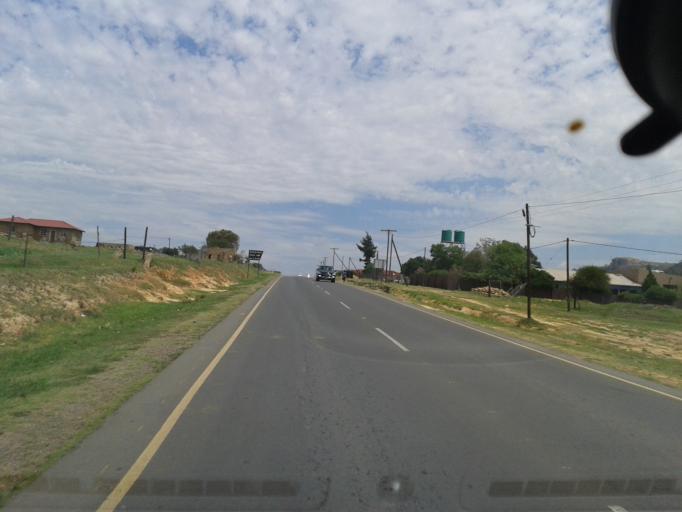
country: LS
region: Maseru
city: Maseru
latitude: -29.3557
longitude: 27.5924
